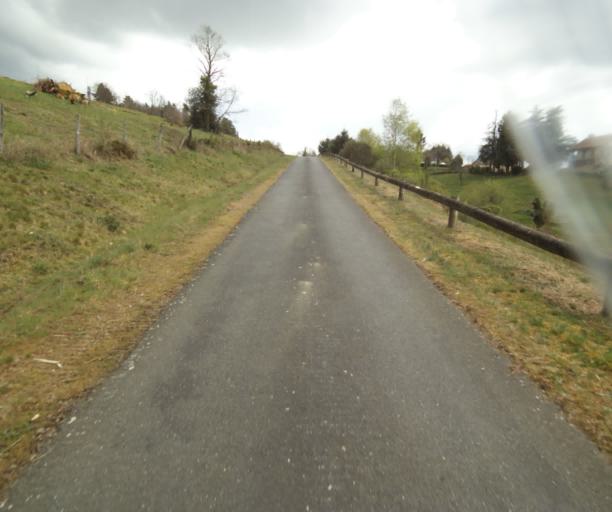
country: FR
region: Limousin
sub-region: Departement de la Correze
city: Naves
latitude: 45.3104
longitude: 1.8111
